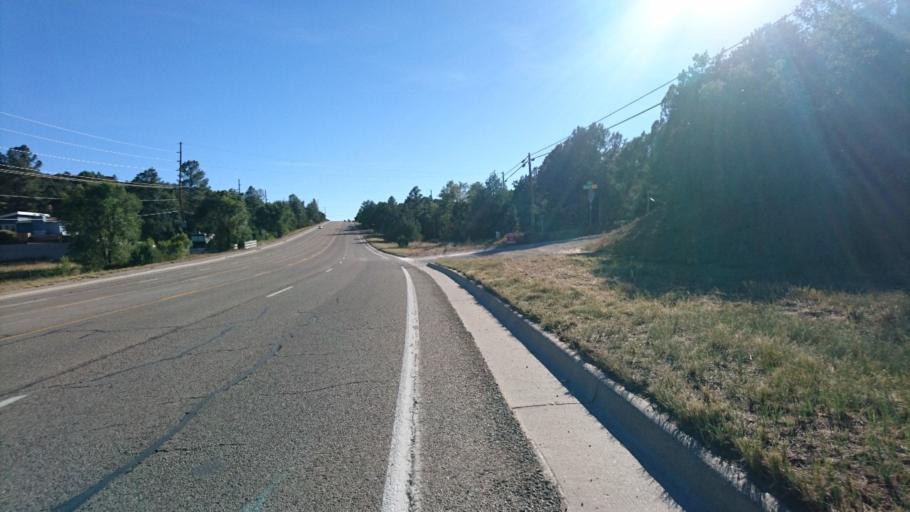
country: US
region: New Mexico
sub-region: Bernalillo County
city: Sandia Knolls
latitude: 35.1543
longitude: -106.3570
